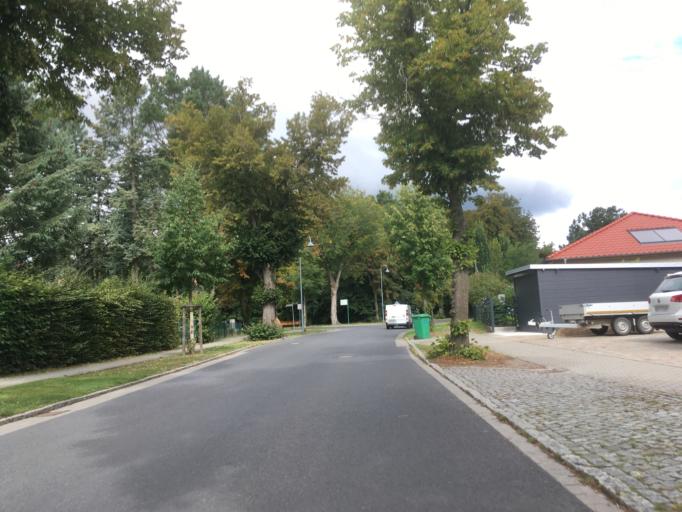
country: DE
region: Brandenburg
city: Wildau
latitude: 52.3084
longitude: 13.7011
